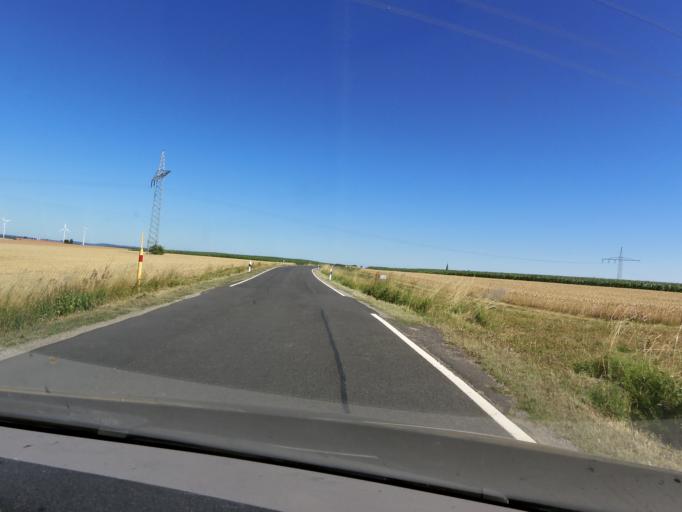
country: DE
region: Bavaria
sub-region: Regierungsbezirk Unterfranken
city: Theilheim
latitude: 49.7496
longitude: 10.0535
